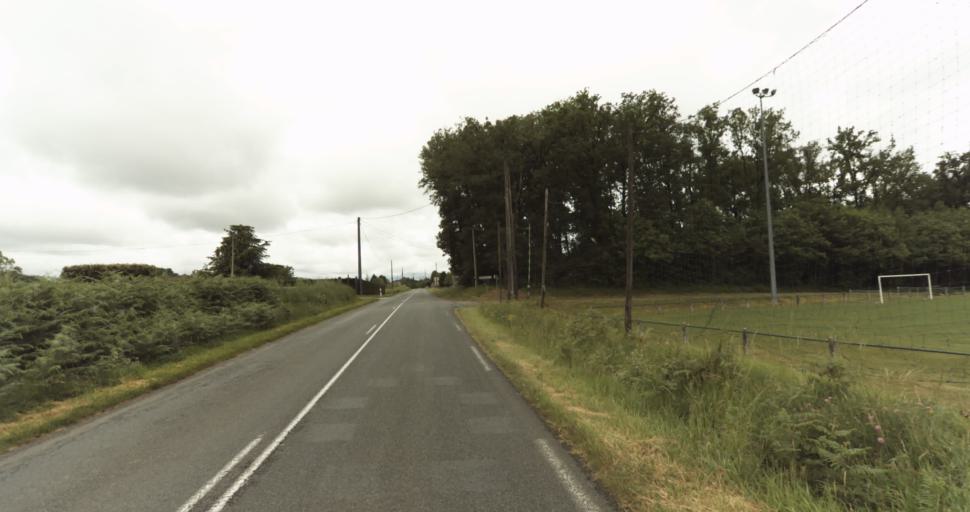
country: FR
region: Aquitaine
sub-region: Departement de la Dordogne
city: Beaumont-du-Perigord
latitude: 44.6933
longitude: 0.8714
